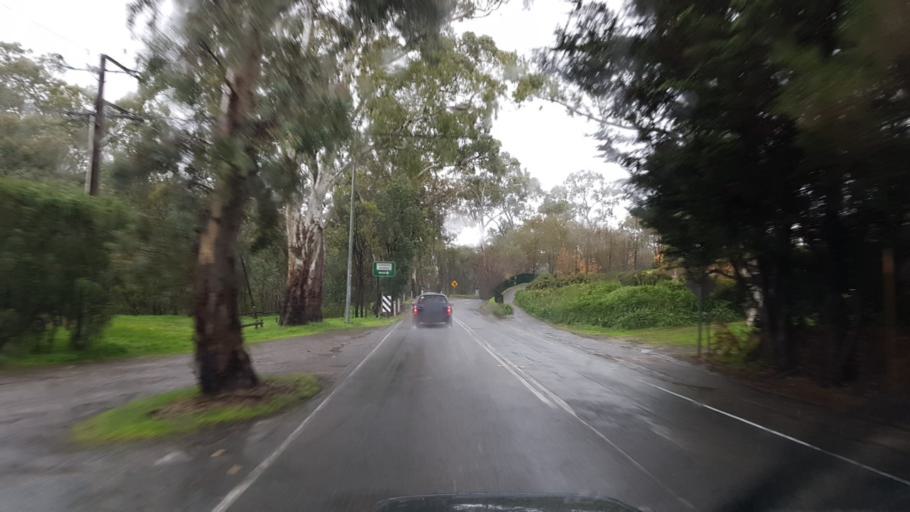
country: AU
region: South Australia
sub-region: Mitcham
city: Blackwood
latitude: -35.0309
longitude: 138.6257
